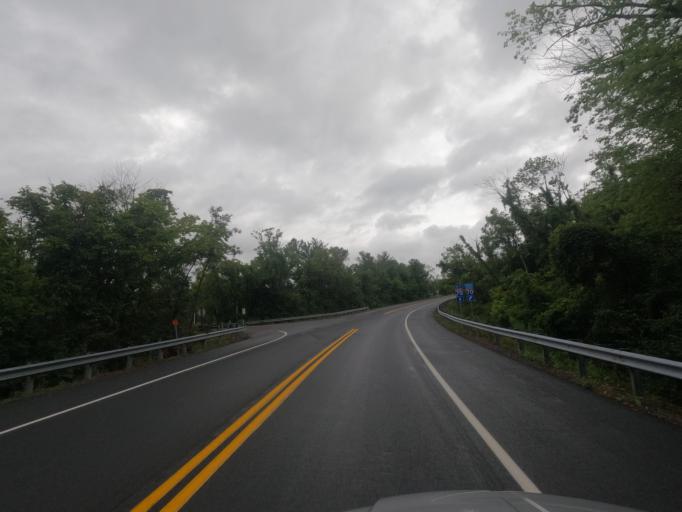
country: US
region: Maryland
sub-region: Washington County
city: Hancock
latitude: 39.6257
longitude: -78.0177
